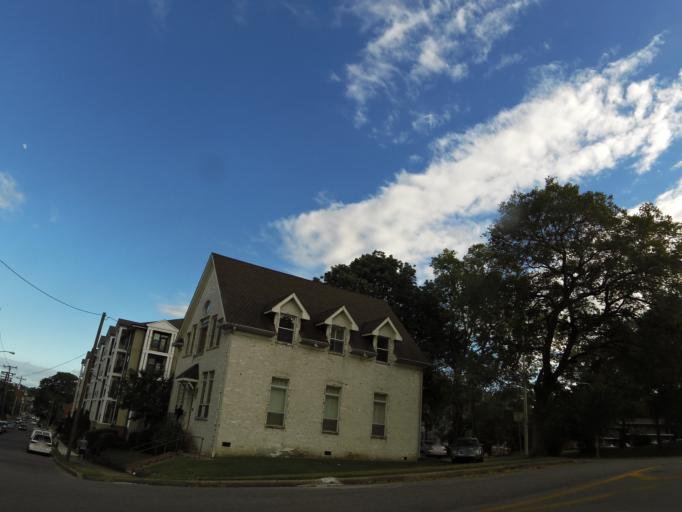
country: US
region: Tennessee
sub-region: Davidson County
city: Nashville
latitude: 36.1482
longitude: -86.8160
